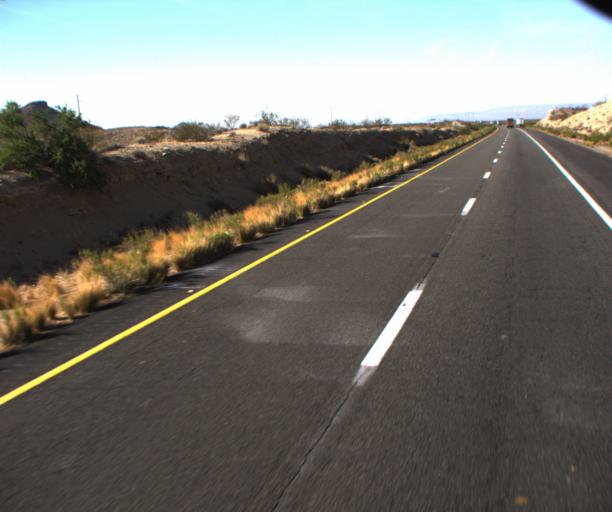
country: US
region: Arizona
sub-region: Mohave County
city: Kingman
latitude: 35.1193
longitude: -114.1129
